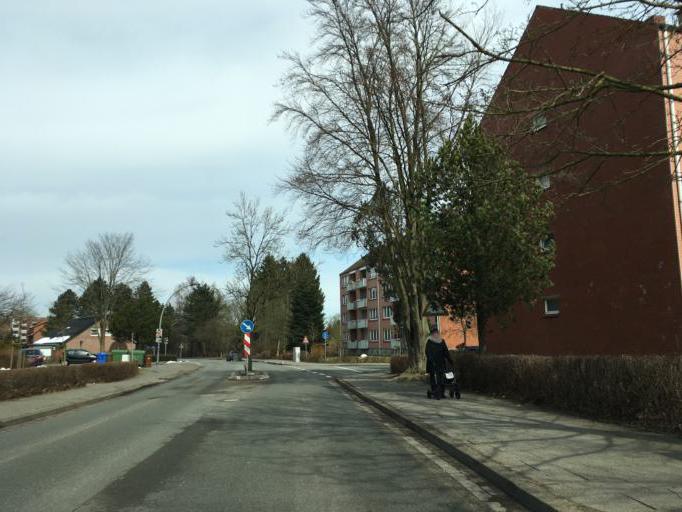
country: DE
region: Schleswig-Holstein
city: Bad Segeberg
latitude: 53.9431
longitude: 10.2955
